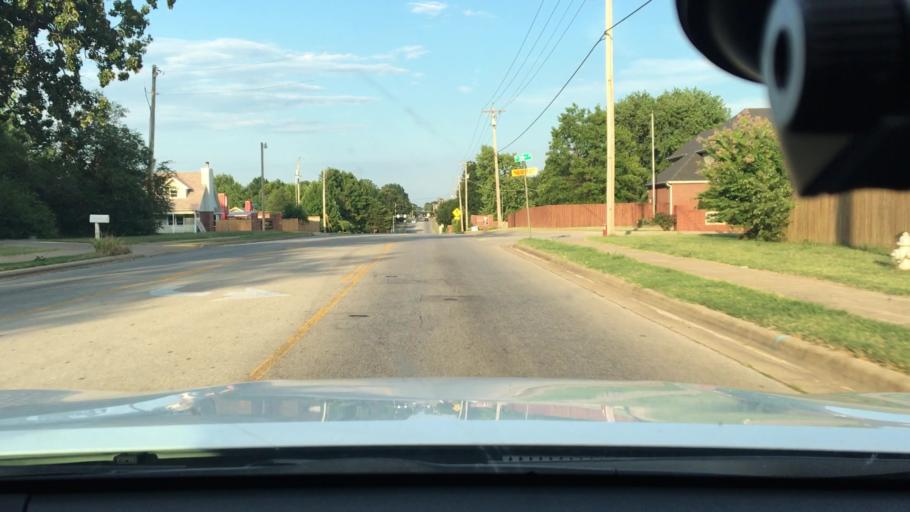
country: US
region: Arkansas
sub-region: Benton County
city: Rogers
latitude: 36.3417
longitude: -94.1611
